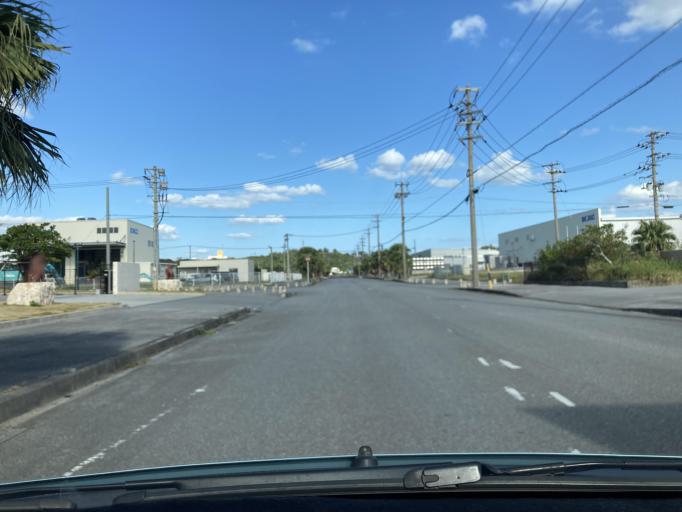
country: JP
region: Okinawa
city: Katsuren-haebaru
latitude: 26.3357
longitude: 127.8644
